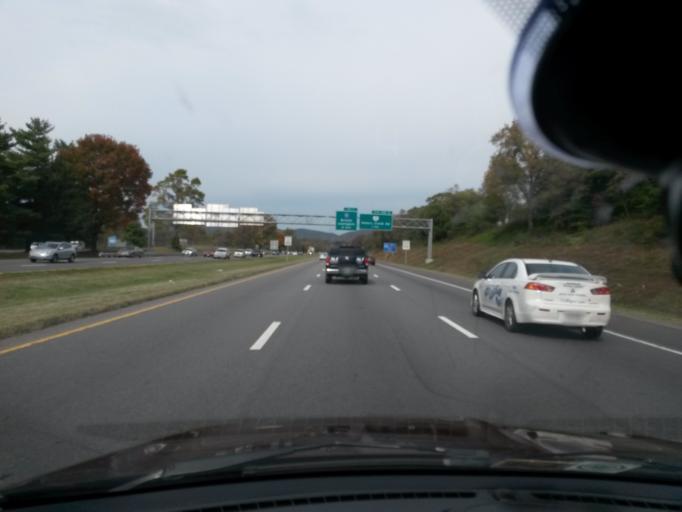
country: US
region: Virginia
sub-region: Roanoke County
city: Hollins
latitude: 37.3123
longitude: -79.9774
